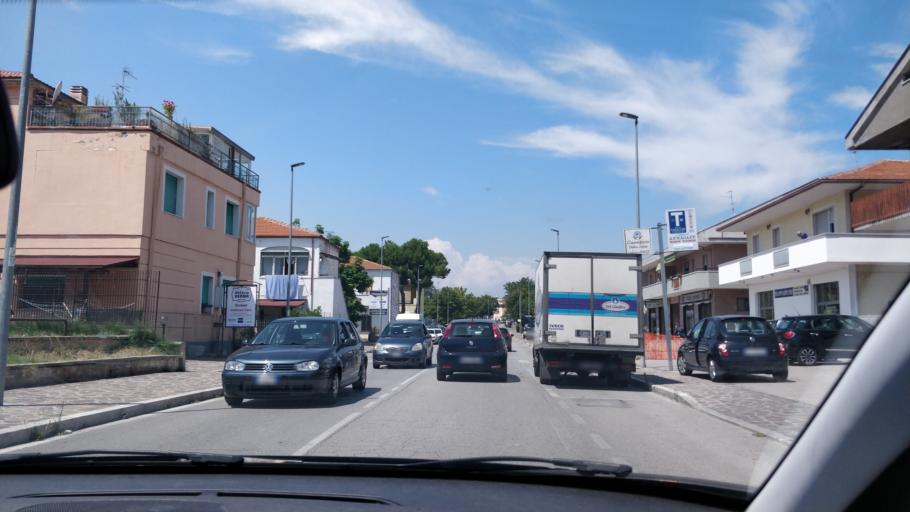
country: IT
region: Abruzzo
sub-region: Provincia di Chieti
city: Francavilla al Mare
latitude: 42.4229
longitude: 14.2820
